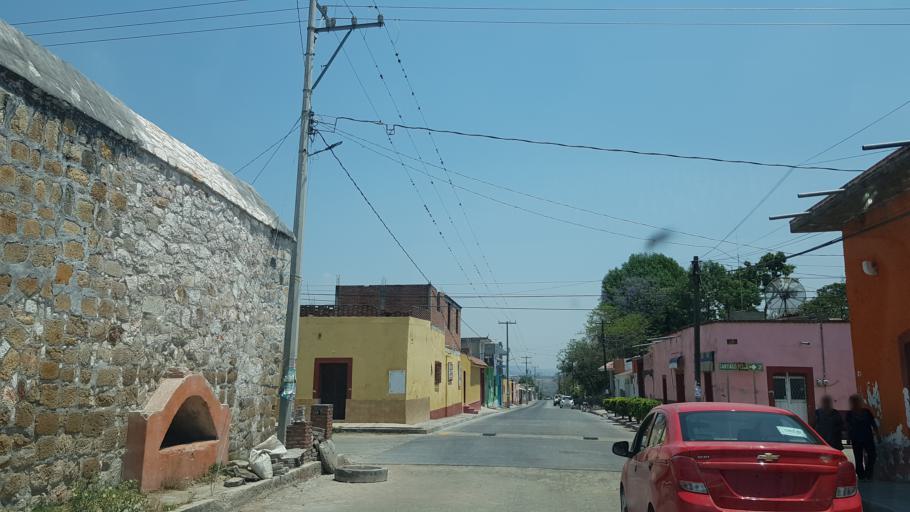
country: MX
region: Puebla
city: Huaquechula
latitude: 18.7686
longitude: -98.5402
